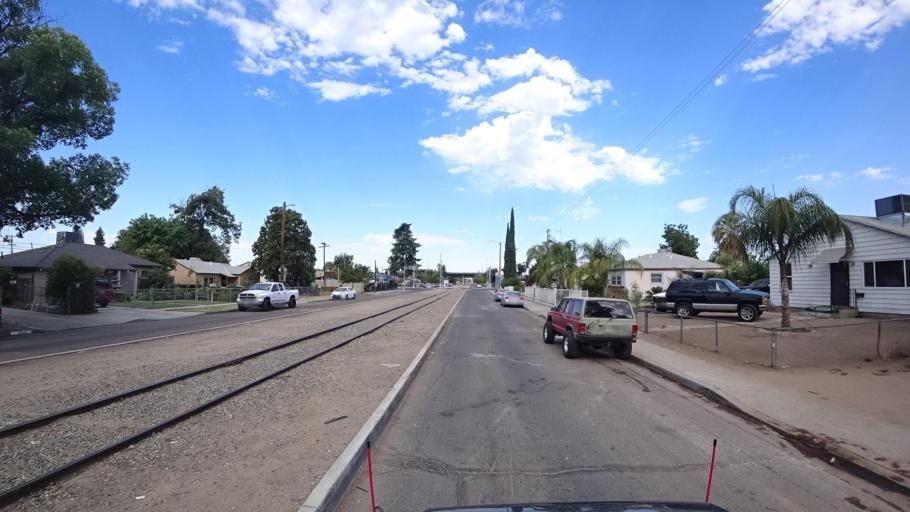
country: US
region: California
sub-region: Fresno County
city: Fresno
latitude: 36.7614
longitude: -119.7713
